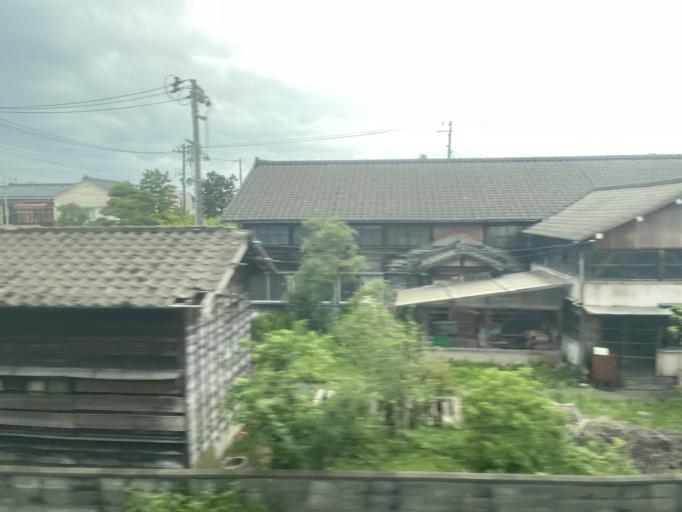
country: JP
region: Niigata
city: Tsubame
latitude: 37.6655
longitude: 138.9334
